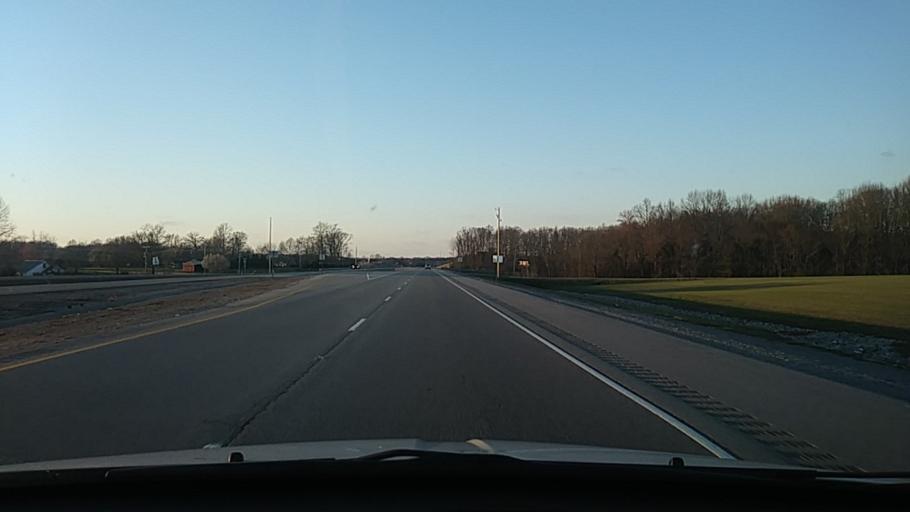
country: US
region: Tennessee
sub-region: Sumner County
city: Portland
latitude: 36.5131
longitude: -86.5058
